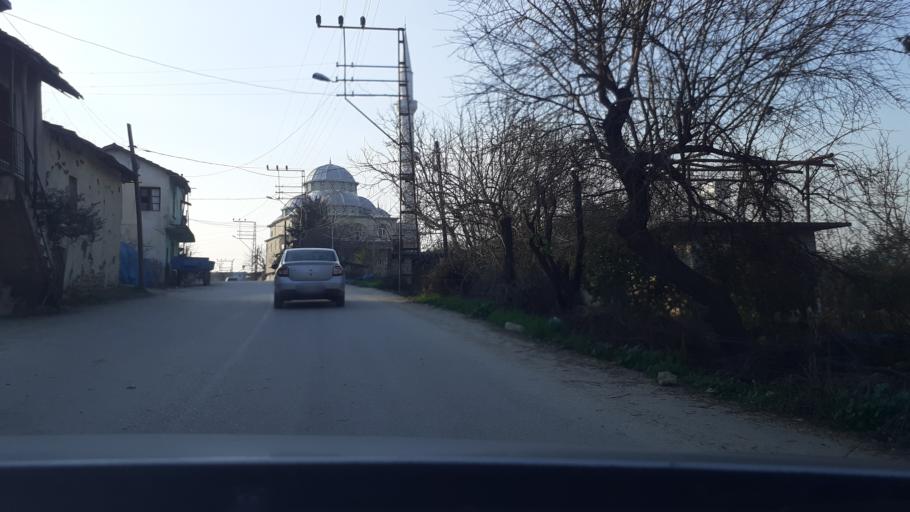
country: TR
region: Hatay
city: Oymakli
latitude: 36.1134
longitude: 36.2941
